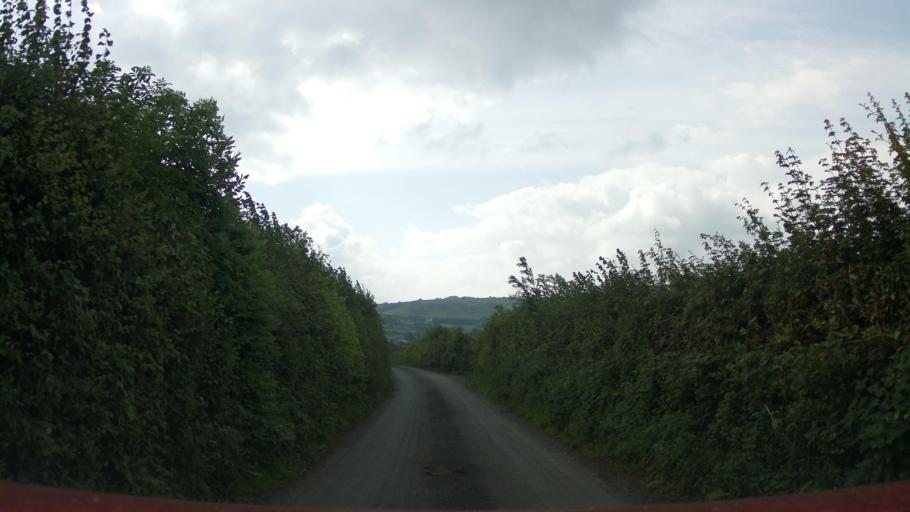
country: GB
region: England
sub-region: Somerset
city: Evercreech
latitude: 51.1445
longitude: -2.4889
